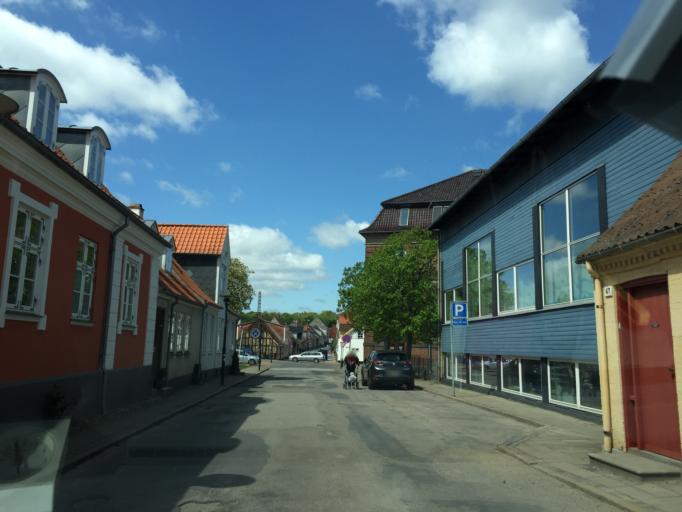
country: DK
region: South Denmark
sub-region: Middelfart Kommune
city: Middelfart
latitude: 55.5045
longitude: 9.7299
